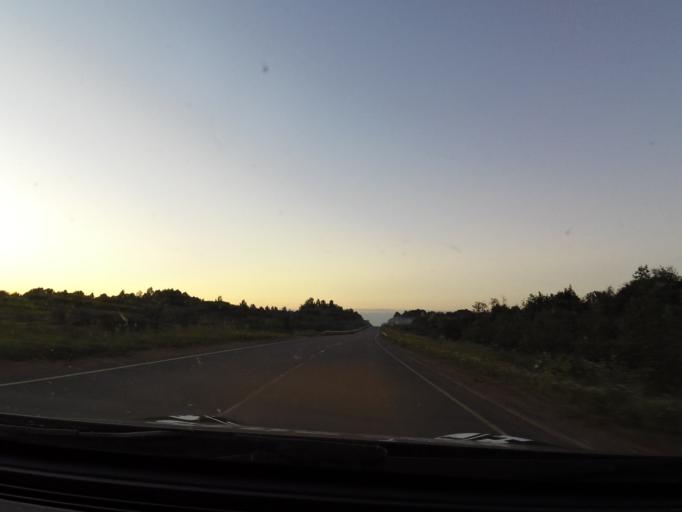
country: RU
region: Vologda
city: Vytegra
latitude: 60.9873
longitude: 36.1083
